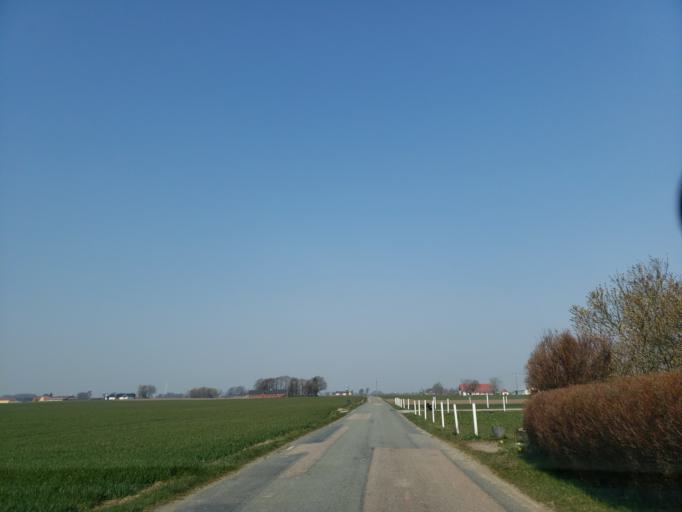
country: SE
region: Skane
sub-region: Simrishamns Kommun
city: Simrishamn
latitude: 55.4485
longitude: 14.2170
